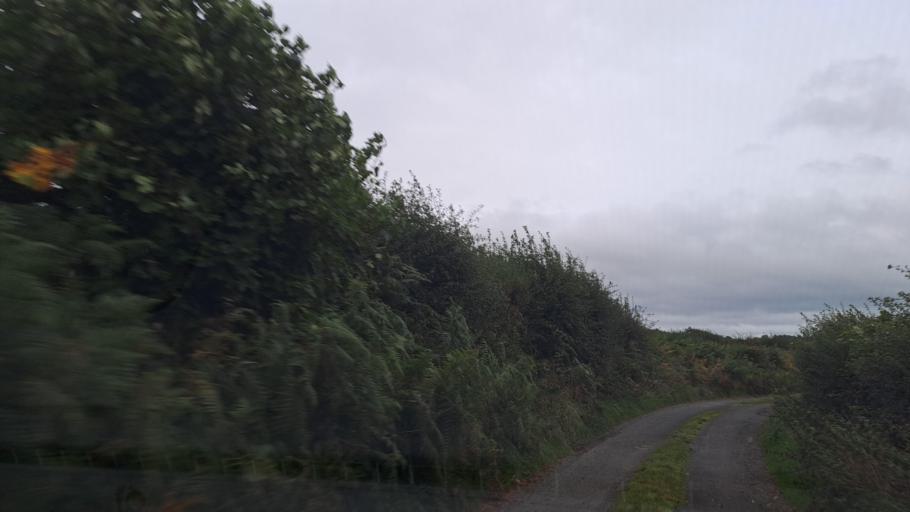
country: IE
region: Ulster
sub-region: An Cabhan
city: Bailieborough
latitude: 53.9799
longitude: -6.9072
